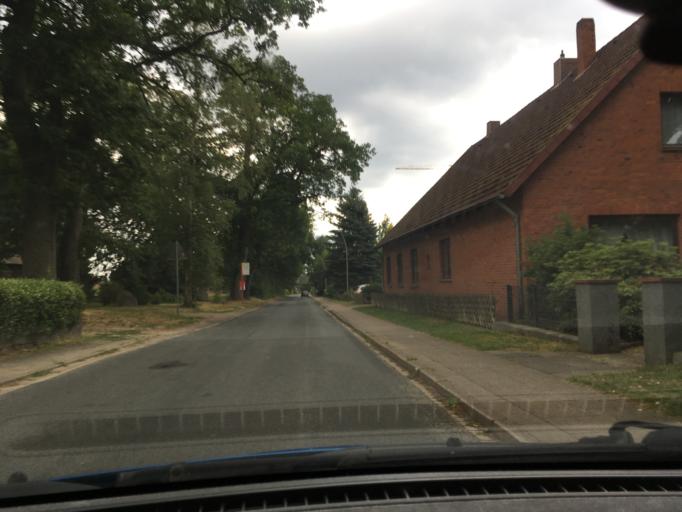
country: DE
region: Lower Saxony
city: Tostedt
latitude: 53.2818
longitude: 9.7381
